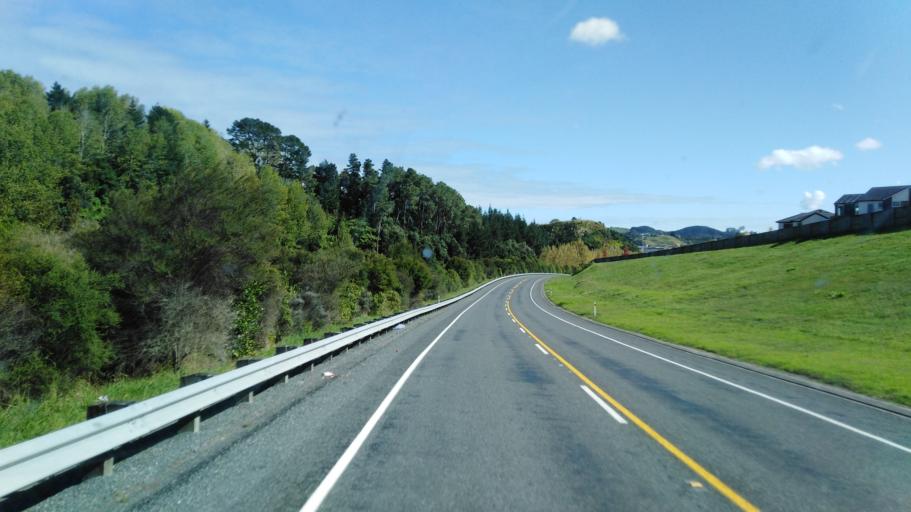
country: NZ
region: Bay of Plenty
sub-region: Tauranga City
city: Tauranga
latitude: -37.7641
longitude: 176.1057
